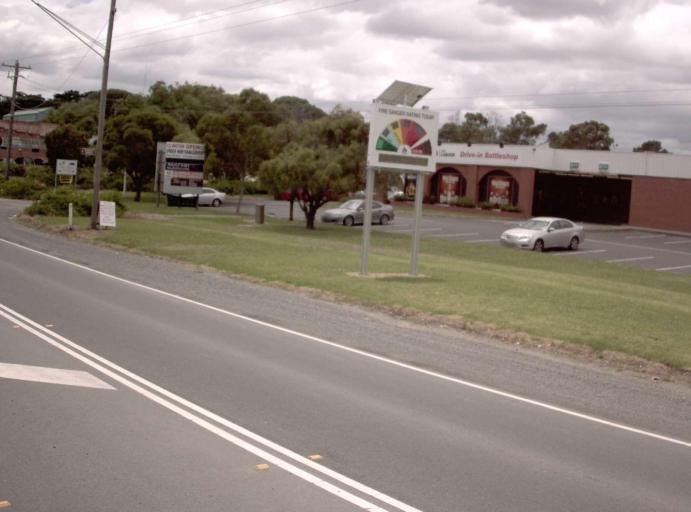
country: AU
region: Victoria
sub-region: Yarra Ranges
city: Lilydale
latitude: -37.7255
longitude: 145.3784
